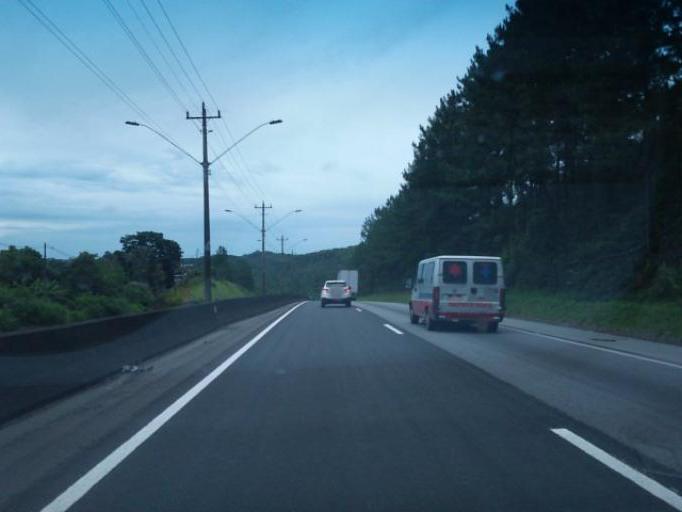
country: BR
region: Sao Paulo
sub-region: Sao Lourenco Da Serra
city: Sao Lourenco da Serra
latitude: -23.8714
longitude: -46.9612
